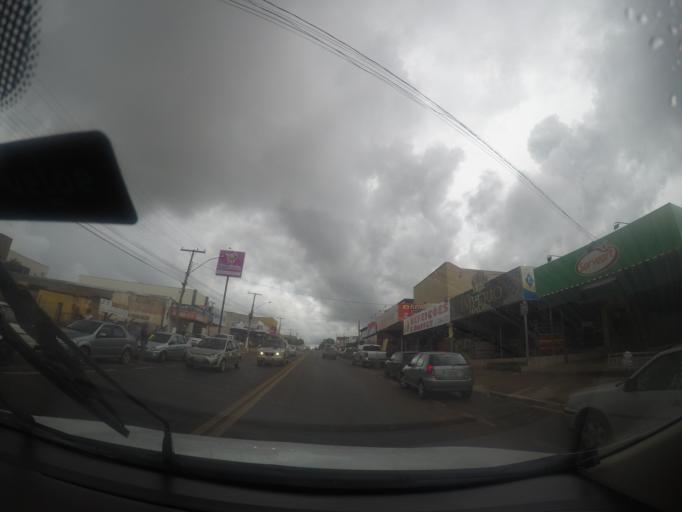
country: BR
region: Goias
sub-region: Trindade
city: Trindade
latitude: -16.6393
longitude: -49.3903
